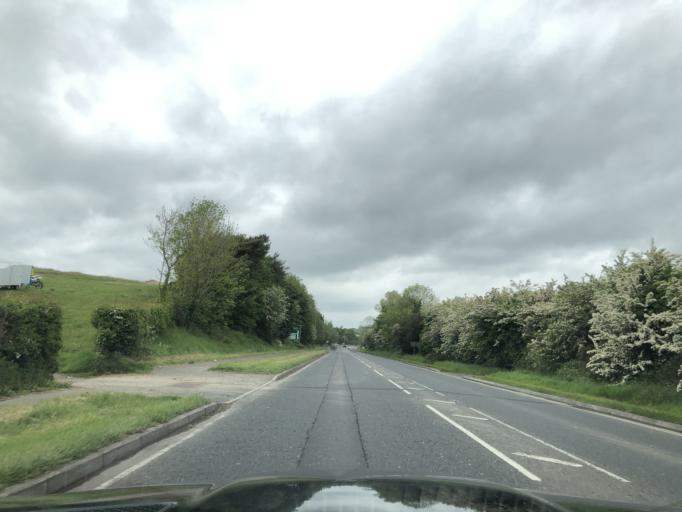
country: GB
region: Northern Ireland
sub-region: Down District
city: Downpatrick
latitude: 54.3504
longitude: -5.7367
